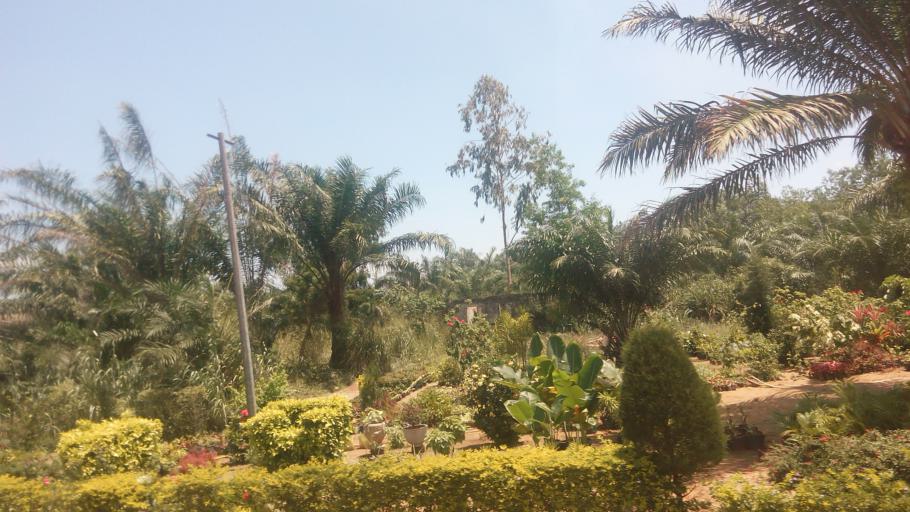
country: BJ
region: Mono
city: Come
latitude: 6.4026
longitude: 1.8971
